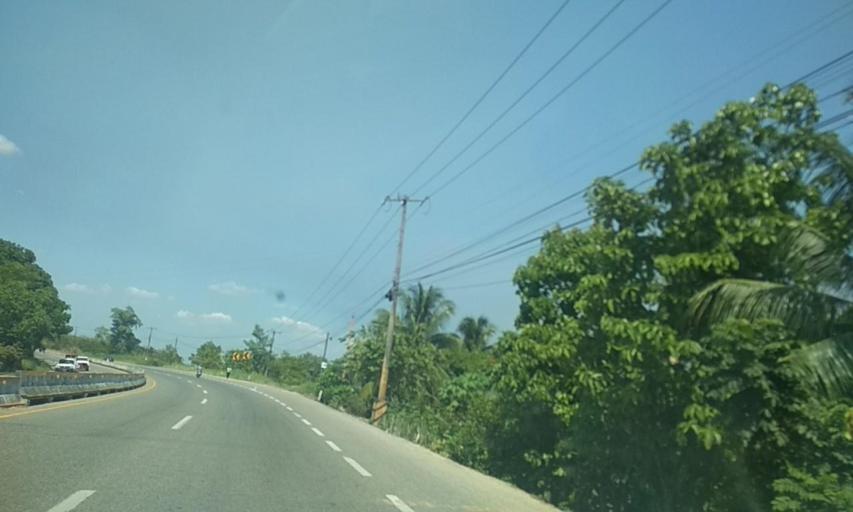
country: MX
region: Tabasco
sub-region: Huimanguillo
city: El Dorado
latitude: 17.8626
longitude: -93.3864
